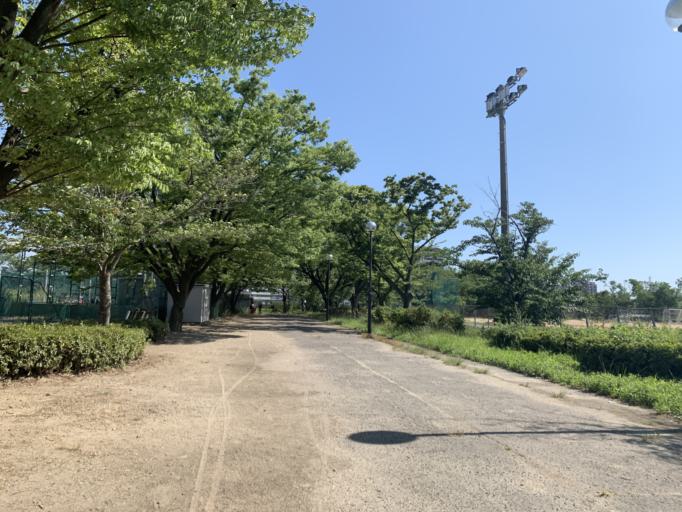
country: JP
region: Osaka
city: Sakai
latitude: 34.5885
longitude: 135.5043
